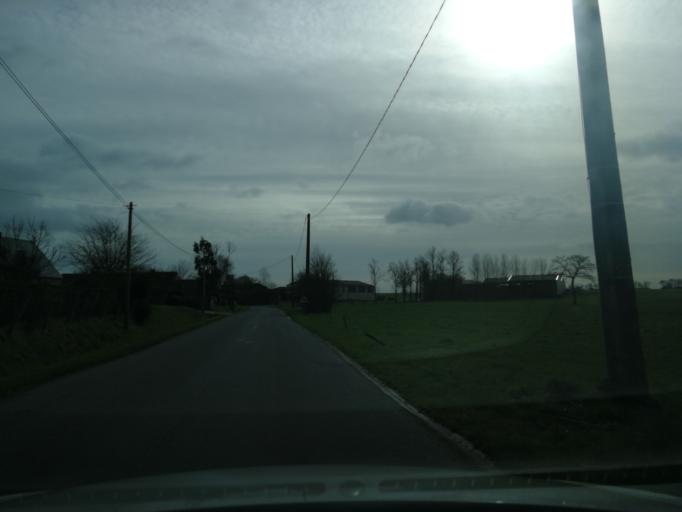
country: FR
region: Brittany
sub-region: Departement d'Ille-et-Vilaine
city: Bourg-des-Comptes
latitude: 47.9149
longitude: -1.7098
